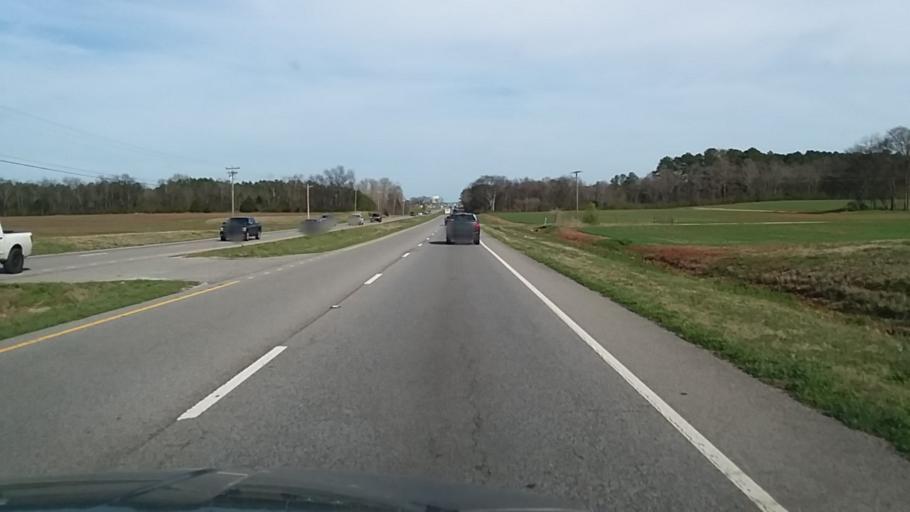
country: US
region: Alabama
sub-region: Morgan County
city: Decatur
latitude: 34.6283
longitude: -86.9302
